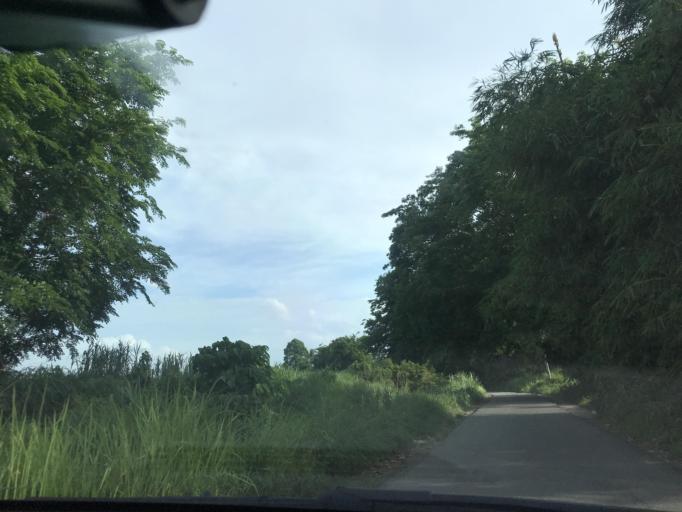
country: MY
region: Kelantan
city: Kota Bharu
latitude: 6.1375
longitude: 102.2246
